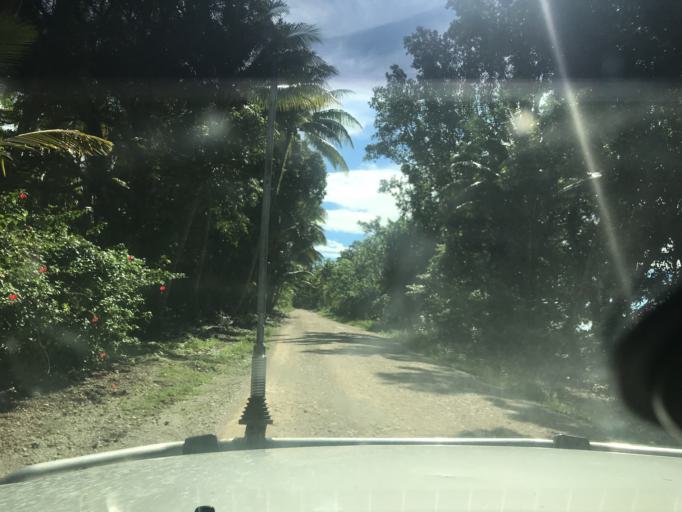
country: SB
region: Malaita
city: Auki
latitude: -8.3638
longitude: 160.6700
